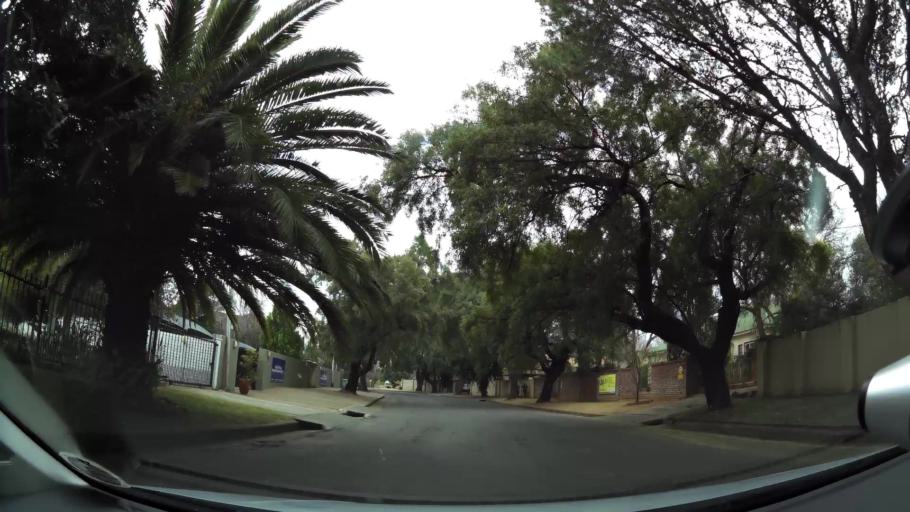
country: ZA
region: Orange Free State
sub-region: Mangaung Metropolitan Municipality
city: Bloemfontein
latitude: -29.1029
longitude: 26.2092
